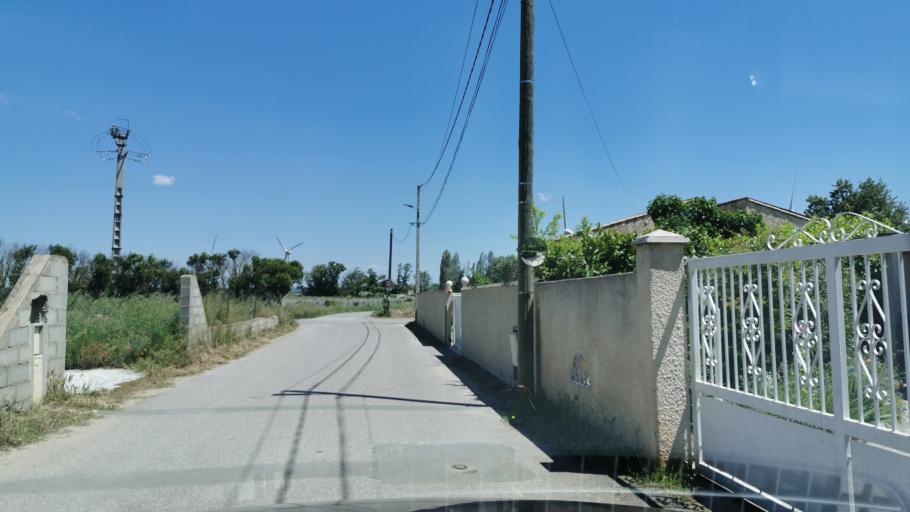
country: FR
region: Languedoc-Roussillon
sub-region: Departement de l'Aude
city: Coursan
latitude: 43.2631
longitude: 3.0237
